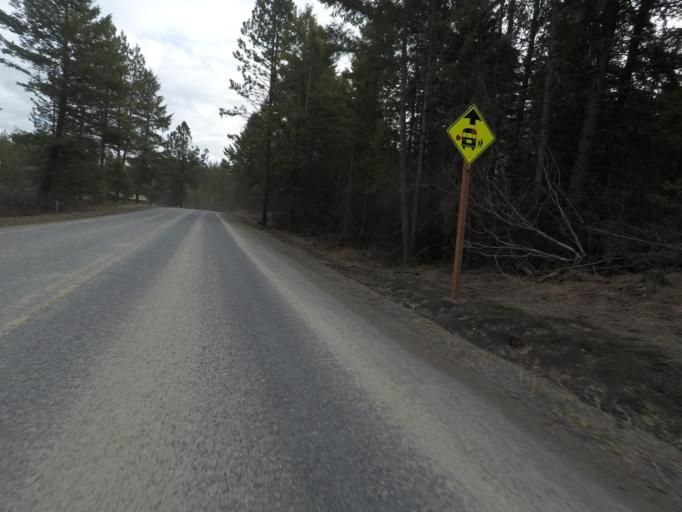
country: US
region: Washington
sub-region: Stevens County
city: Colville
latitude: 48.5035
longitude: -117.8546
